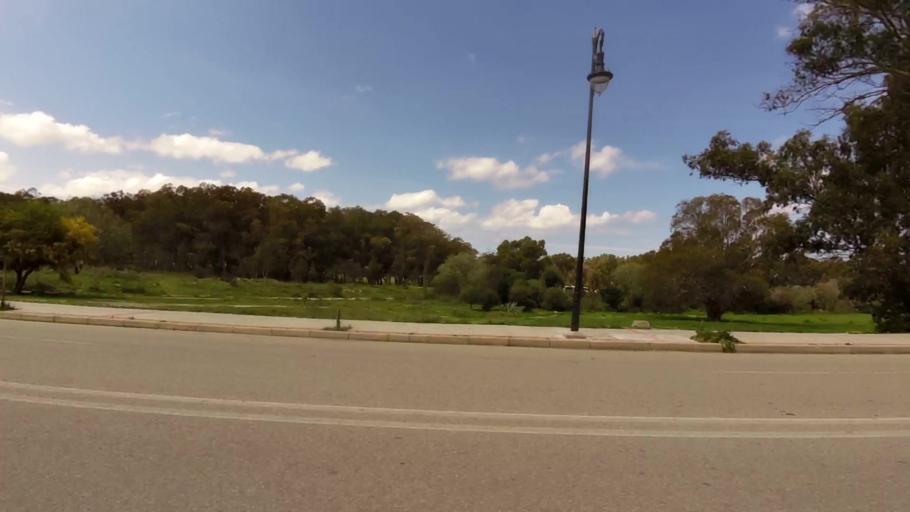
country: MA
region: Tanger-Tetouan
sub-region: Tanger-Assilah
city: Tangier
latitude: 35.7795
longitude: -5.7614
